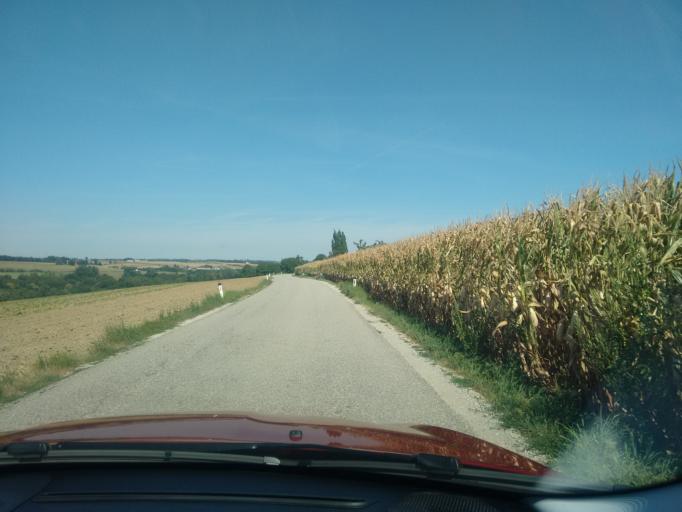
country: AT
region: Upper Austria
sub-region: Wels-Land
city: Steinhaus
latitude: 48.1083
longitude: 14.0261
